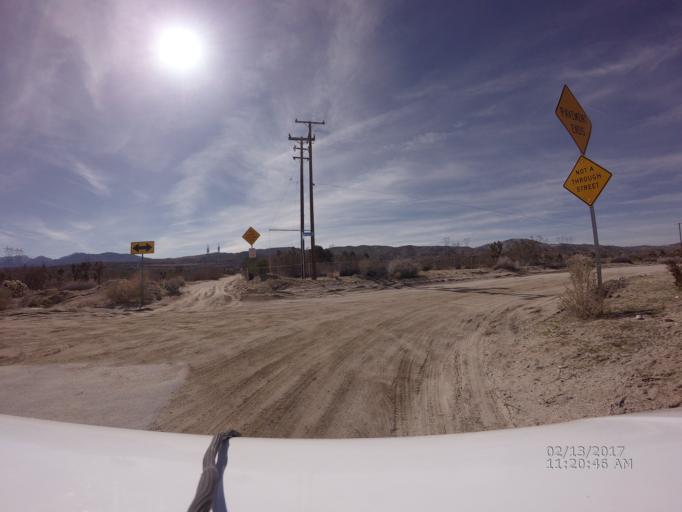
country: US
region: California
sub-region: Los Angeles County
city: Littlerock
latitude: 34.5138
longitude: -117.9925
